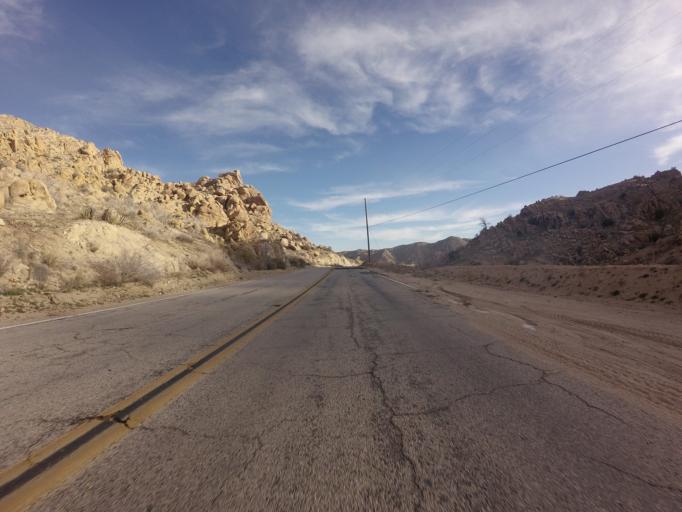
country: US
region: California
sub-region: San Bernardino County
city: Yucca Valley
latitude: 34.1356
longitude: -116.4657
